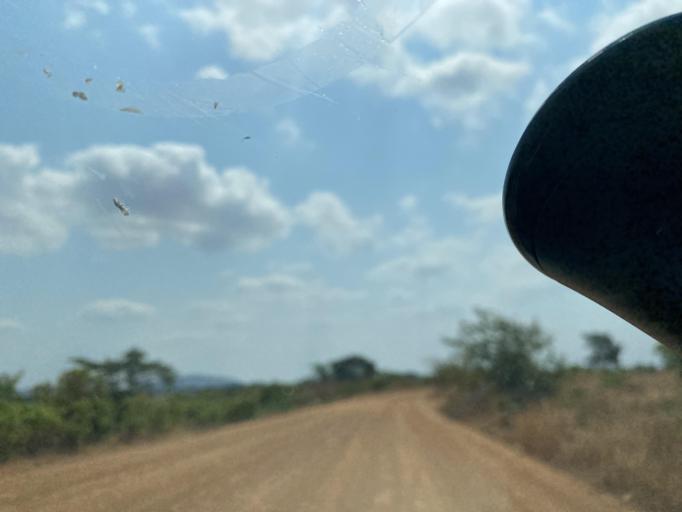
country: ZM
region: Lusaka
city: Chongwe
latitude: -15.5928
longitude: 28.7934
